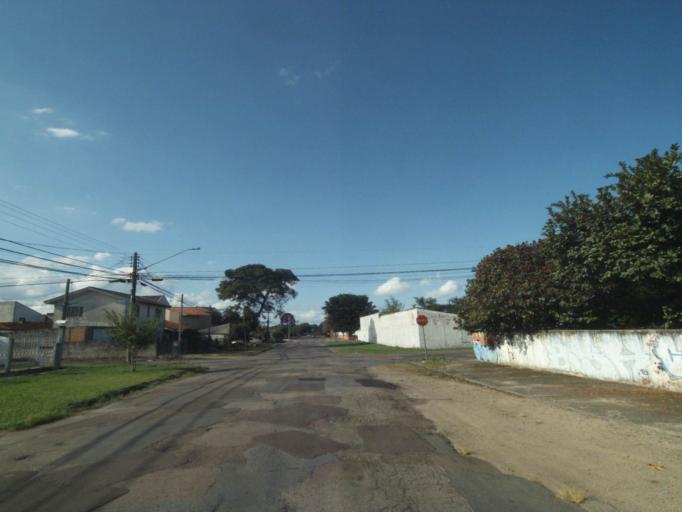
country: BR
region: Parana
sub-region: Pinhais
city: Pinhais
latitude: -25.4417
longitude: -49.2115
